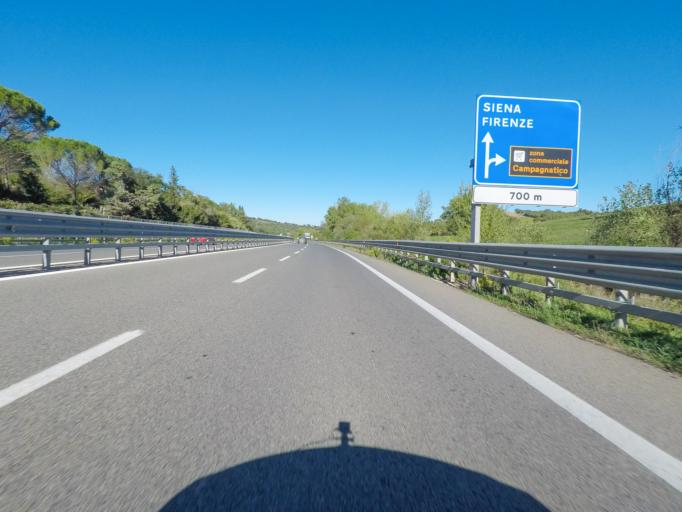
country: IT
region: Tuscany
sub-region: Provincia di Grosseto
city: Campagnatico
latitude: 42.8803
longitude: 11.2171
